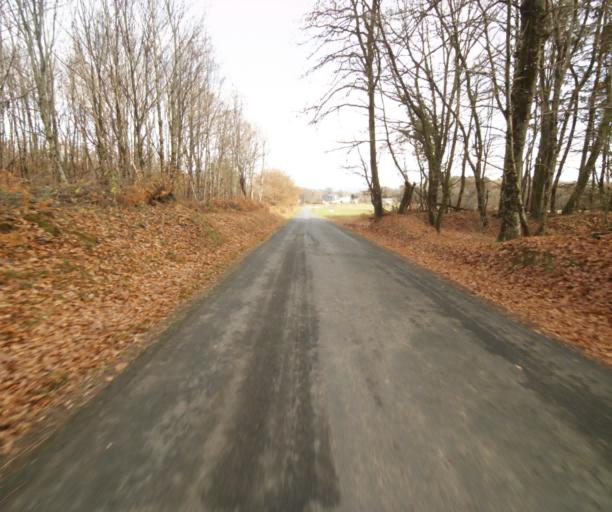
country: FR
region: Limousin
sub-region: Departement de la Correze
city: Chameyrat
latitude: 45.2519
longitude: 1.6987
